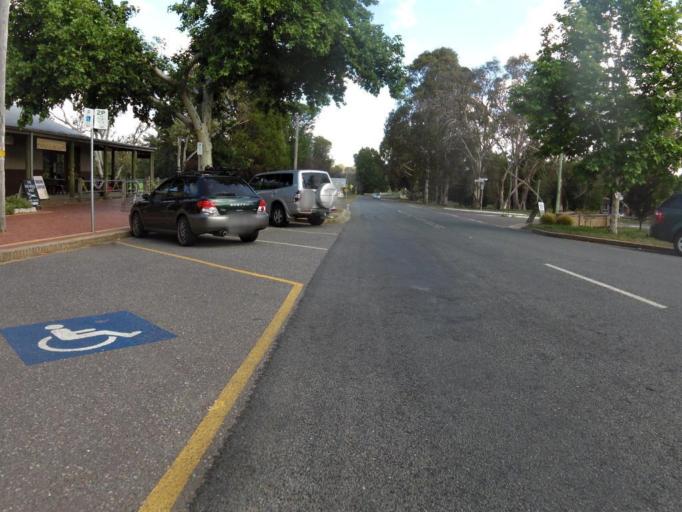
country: AU
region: Australian Capital Territory
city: Belconnen
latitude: -35.1708
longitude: 149.0703
